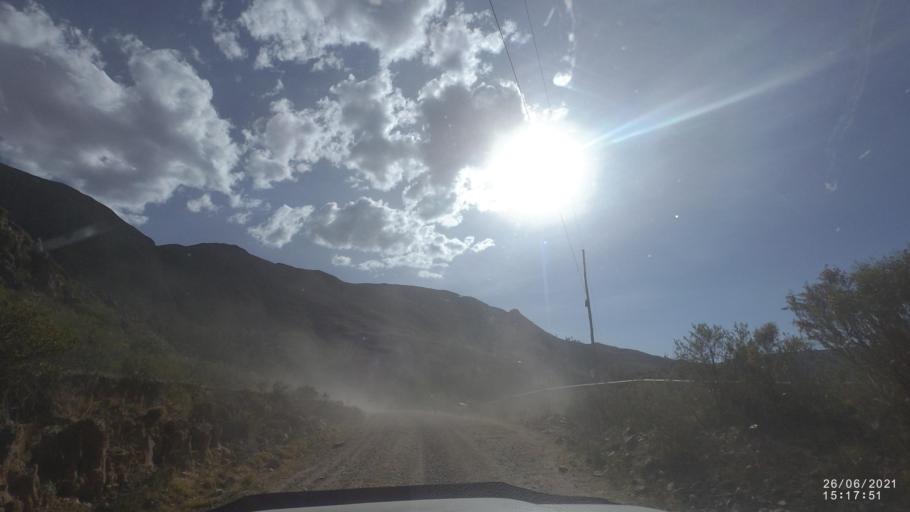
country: BO
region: Cochabamba
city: Mizque
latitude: -17.9506
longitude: -65.6533
